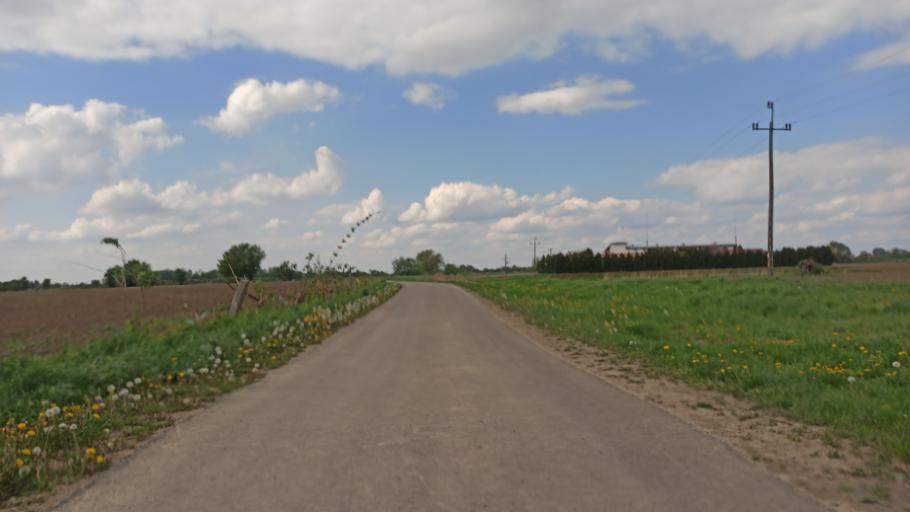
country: PL
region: Subcarpathian Voivodeship
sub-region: Powiat jaroslawski
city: Radymno
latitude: 49.9601
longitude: 22.8105
